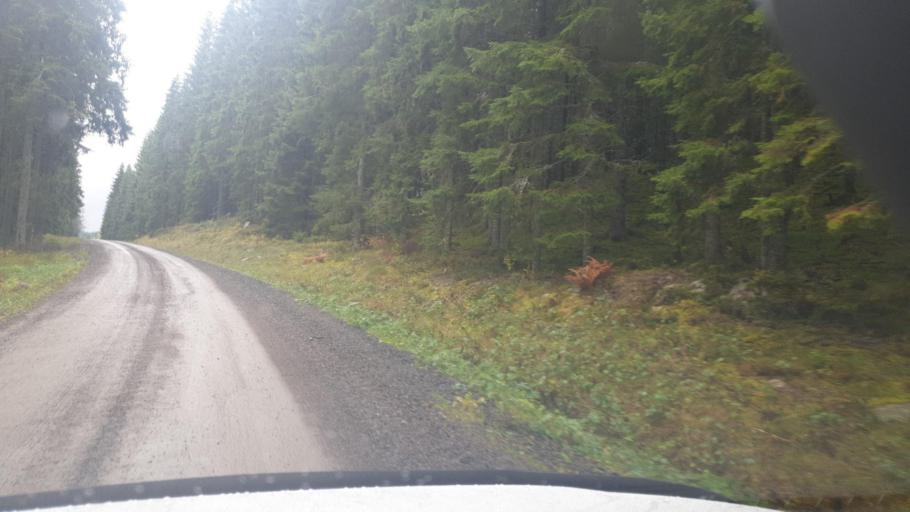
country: SE
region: Vaermland
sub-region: Sunne Kommun
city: Sunne
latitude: 59.8602
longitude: 12.8666
